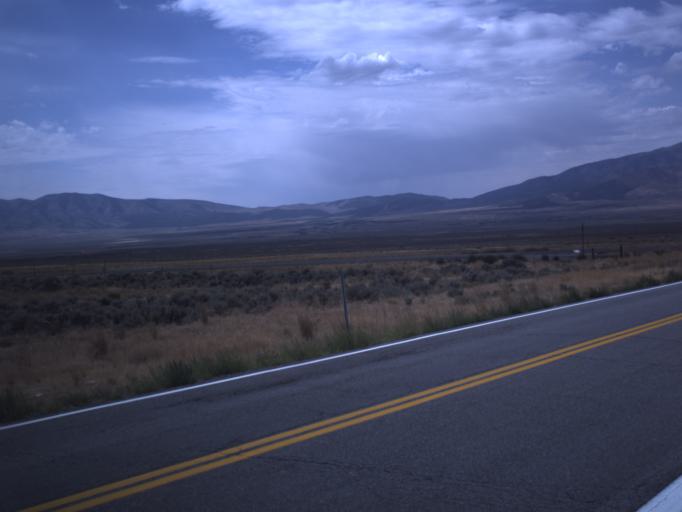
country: US
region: Utah
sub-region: Tooele County
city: Tooele
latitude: 40.3601
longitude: -112.3267
